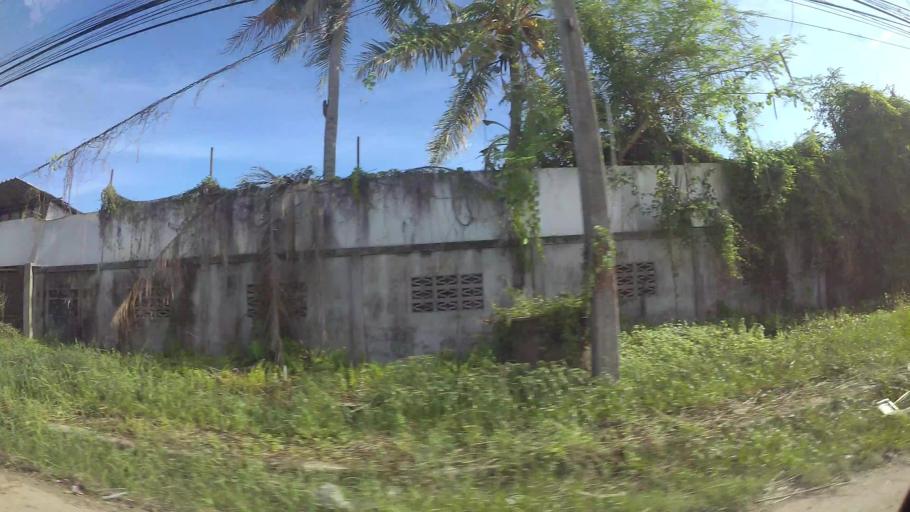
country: TH
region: Rayong
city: Rayong
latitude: 12.6805
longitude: 101.2993
